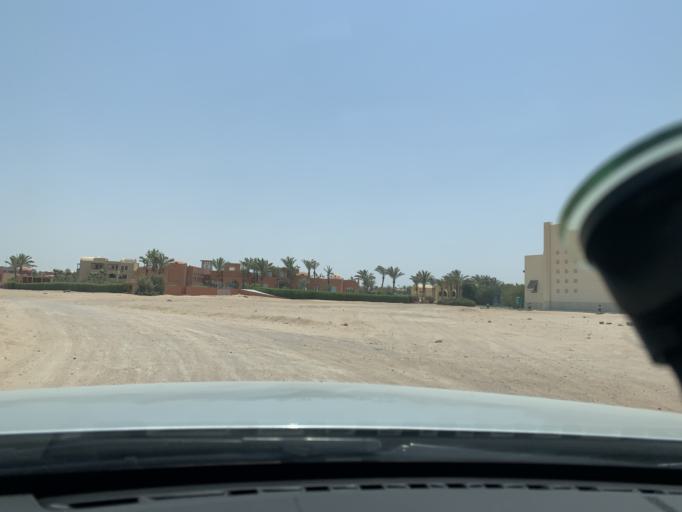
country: EG
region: Red Sea
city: El Gouna
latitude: 27.3989
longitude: 33.6712
